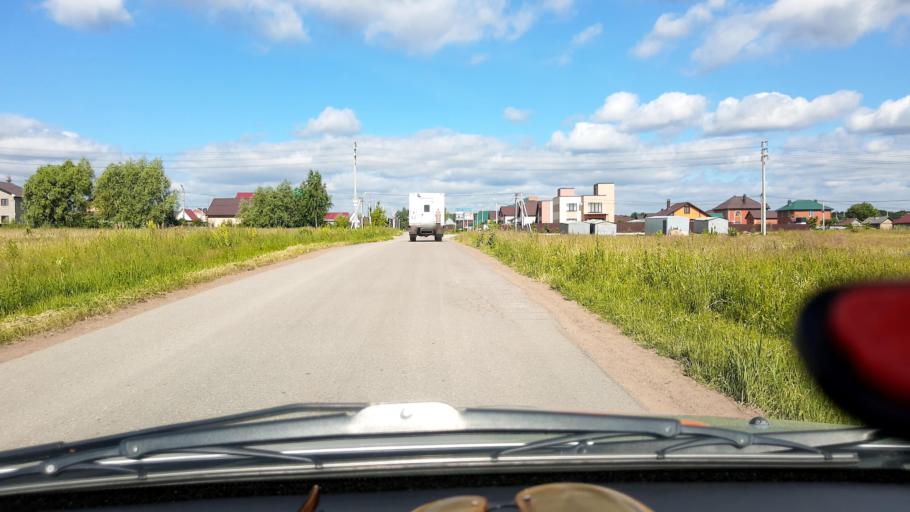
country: RU
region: Bashkortostan
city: Kabakovo
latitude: 54.6189
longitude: 56.0879
